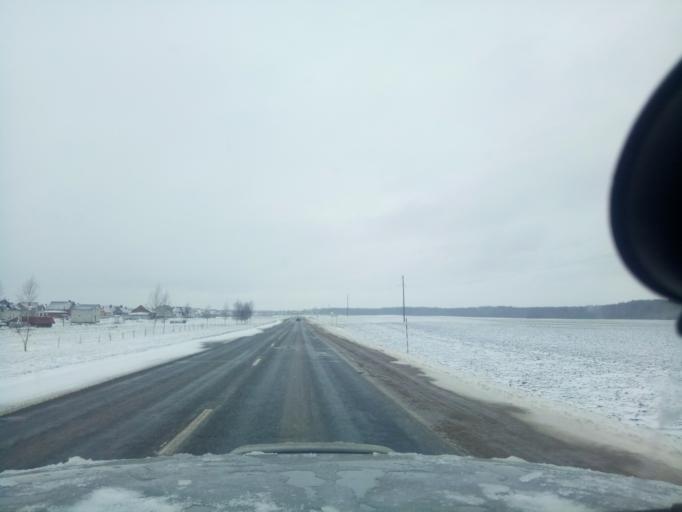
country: BY
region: Minsk
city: Nyasvizh
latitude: 53.2223
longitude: 26.6474
